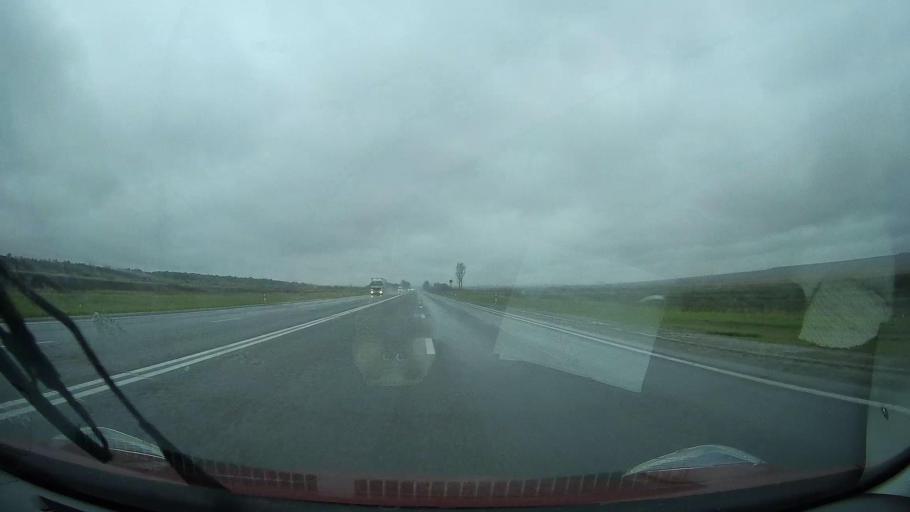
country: RU
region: Stavropol'skiy
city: Nevinnomyssk
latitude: 44.6283
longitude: 42.0419
